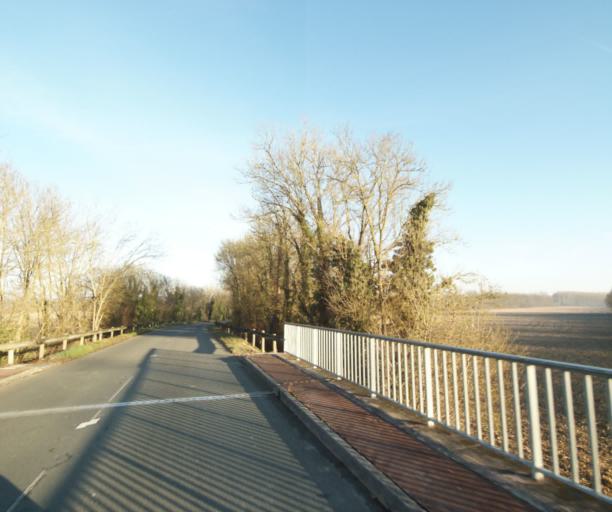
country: FR
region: Poitou-Charentes
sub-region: Departement de la Charente-Maritime
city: Cherac
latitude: 45.6790
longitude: -0.4626
